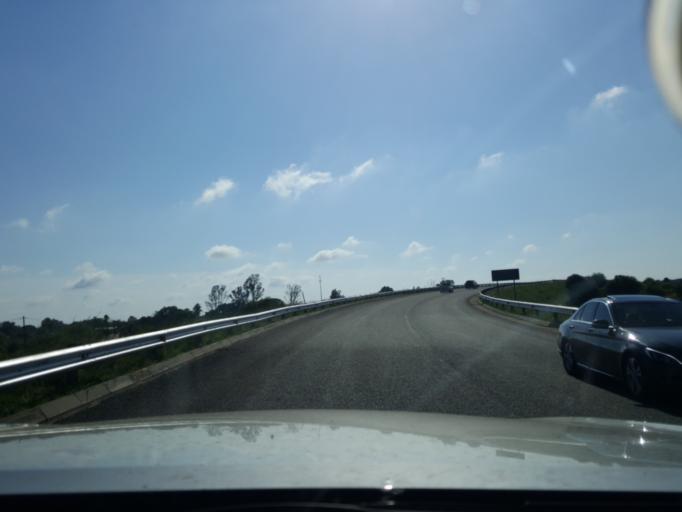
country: ZA
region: North-West
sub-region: Ngaka Modiri Molema District Municipality
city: Zeerust
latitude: -25.7542
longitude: 25.9589
